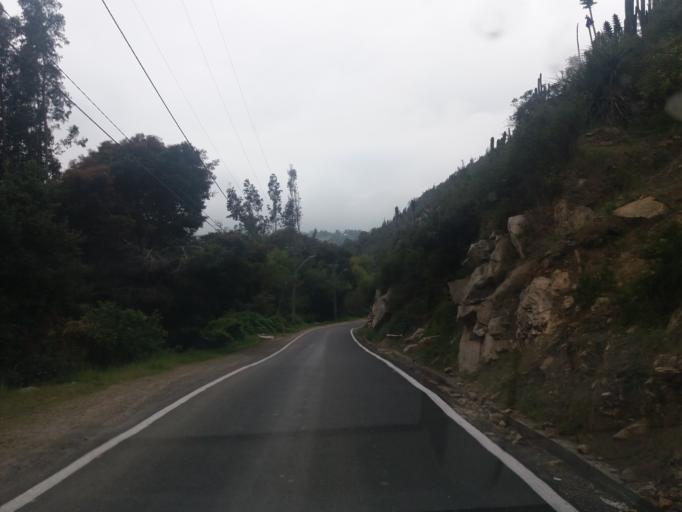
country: CL
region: Valparaiso
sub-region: Provincia de Marga Marga
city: Limache
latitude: -33.0317
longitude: -71.0839
